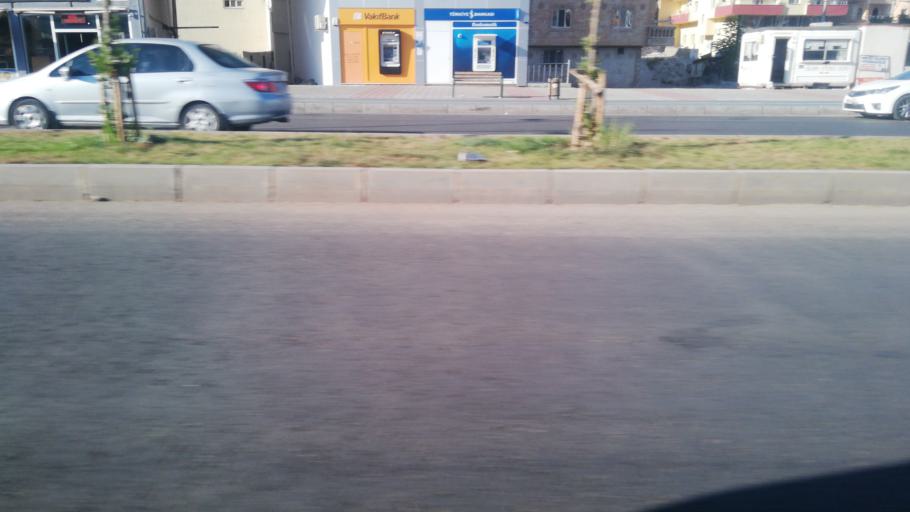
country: TR
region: Mardin
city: Midyat
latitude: 37.4182
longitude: 41.3568
